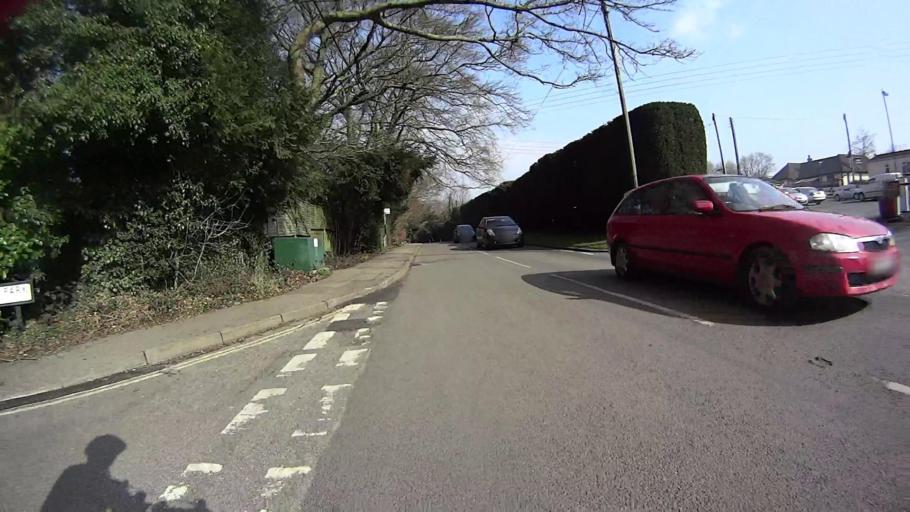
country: GB
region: England
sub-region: Surrey
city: Headley
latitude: 51.2511
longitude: -0.2859
